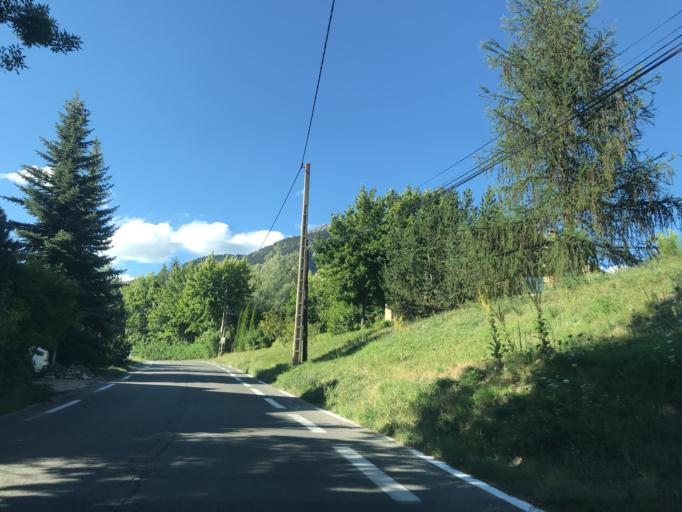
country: FR
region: Provence-Alpes-Cote d'Azur
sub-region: Departement des Hautes-Alpes
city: Briancon
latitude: 44.8915
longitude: 6.6407
